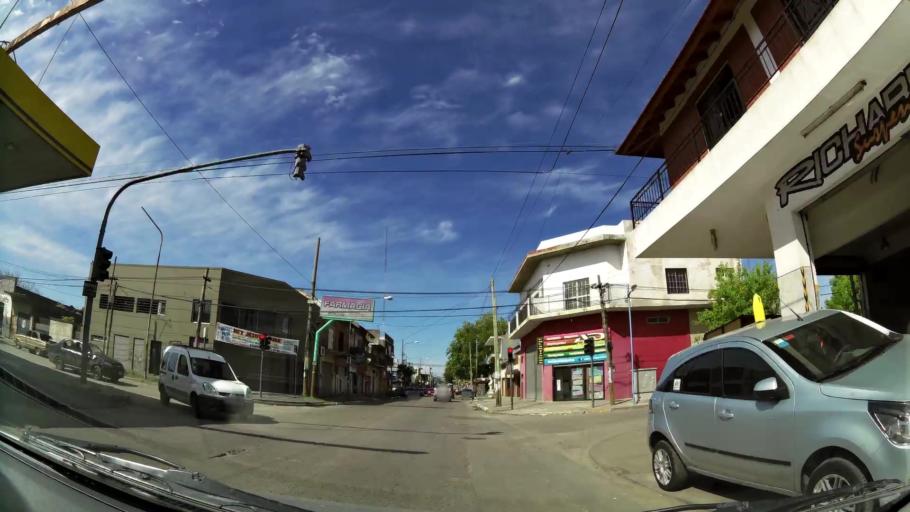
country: AR
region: Buenos Aires
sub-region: Partido de Quilmes
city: Quilmes
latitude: -34.7706
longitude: -58.2956
